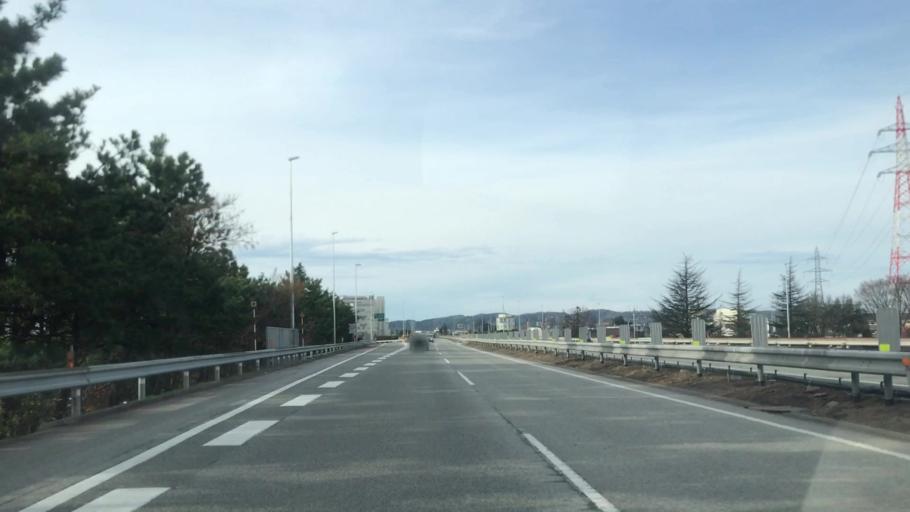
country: JP
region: Toyama
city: Toyama-shi
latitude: 36.6537
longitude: 137.2073
